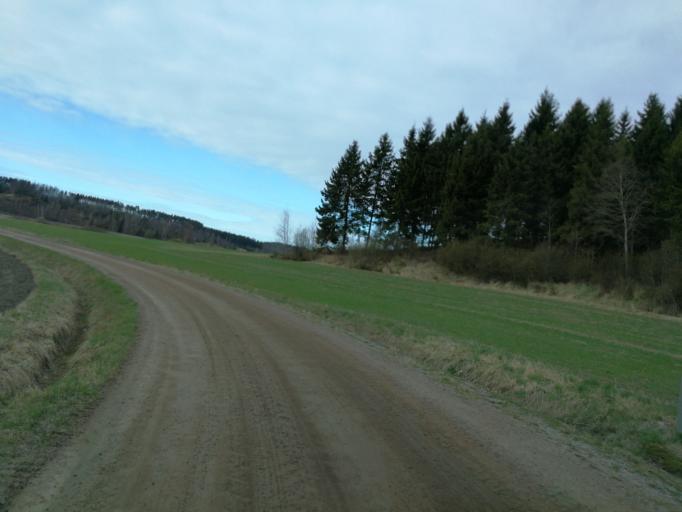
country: FI
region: Varsinais-Suomi
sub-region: Salo
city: Muurla
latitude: 60.3319
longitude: 23.2552
